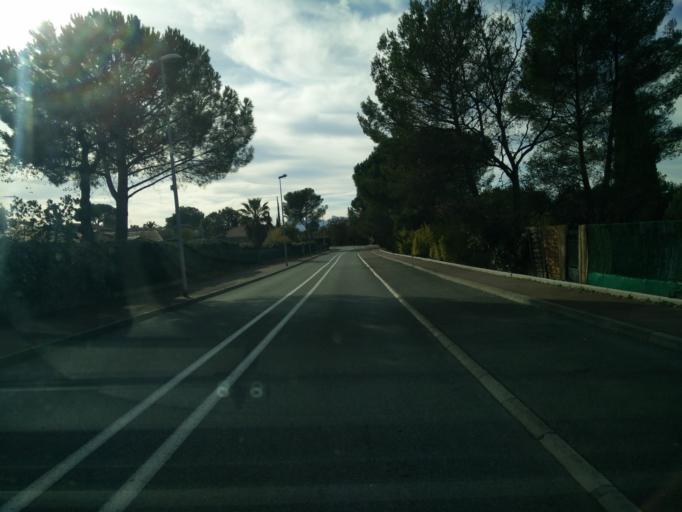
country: FR
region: Provence-Alpes-Cote d'Azur
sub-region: Departement du Var
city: Puget-sur-Argens
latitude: 43.4981
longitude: 6.6426
